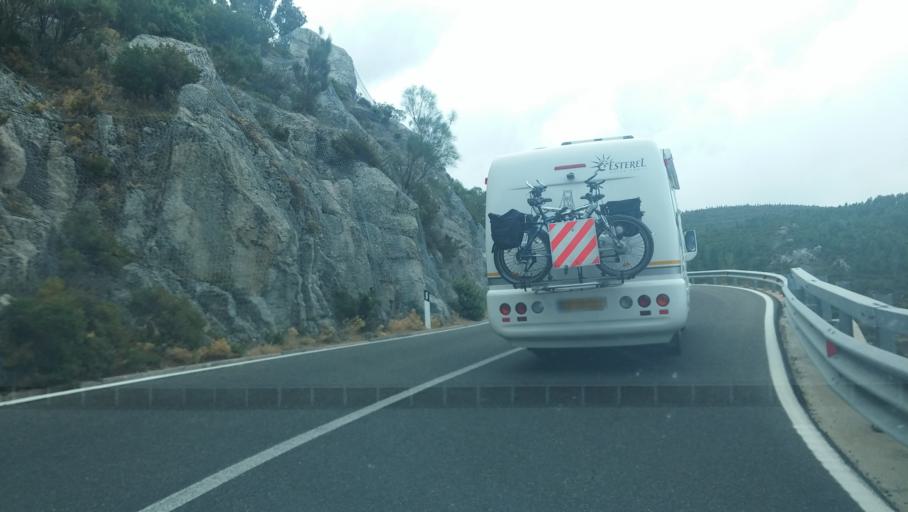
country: IT
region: Sardinia
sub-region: Provincia di Ogliastra
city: Urzulei
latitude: 40.1757
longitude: 9.5273
